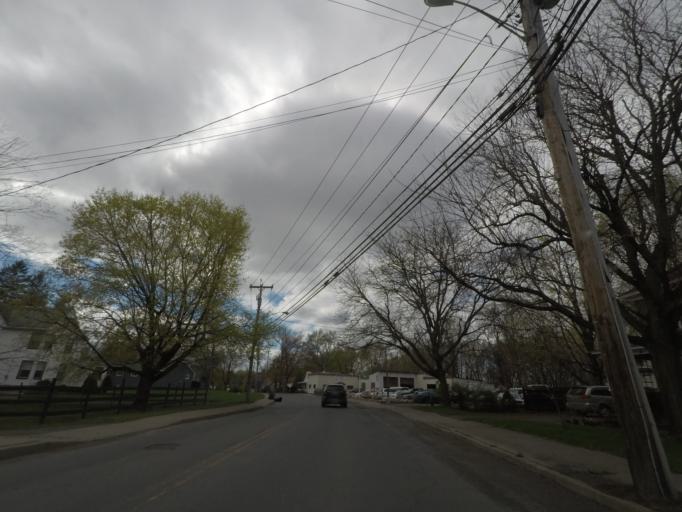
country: US
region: New York
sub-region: Columbia County
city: Chatham
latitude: 42.3578
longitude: -73.6053
